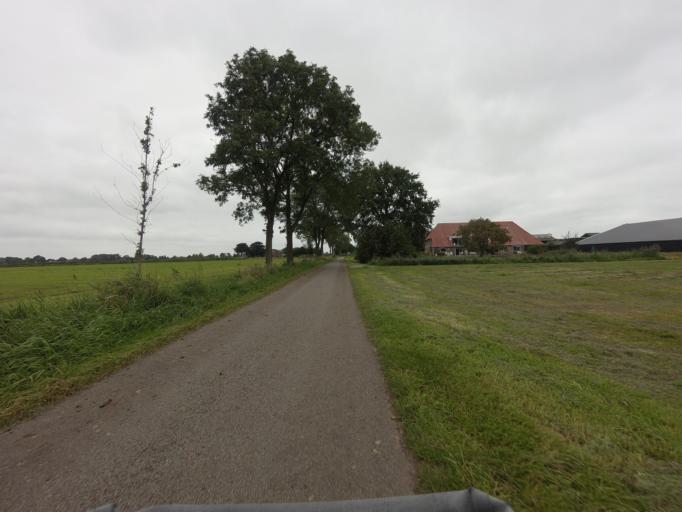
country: NL
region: Overijssel
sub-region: Gemeente Steenwijkerland
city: Blokzijl
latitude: 52.7392
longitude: 6.0070
